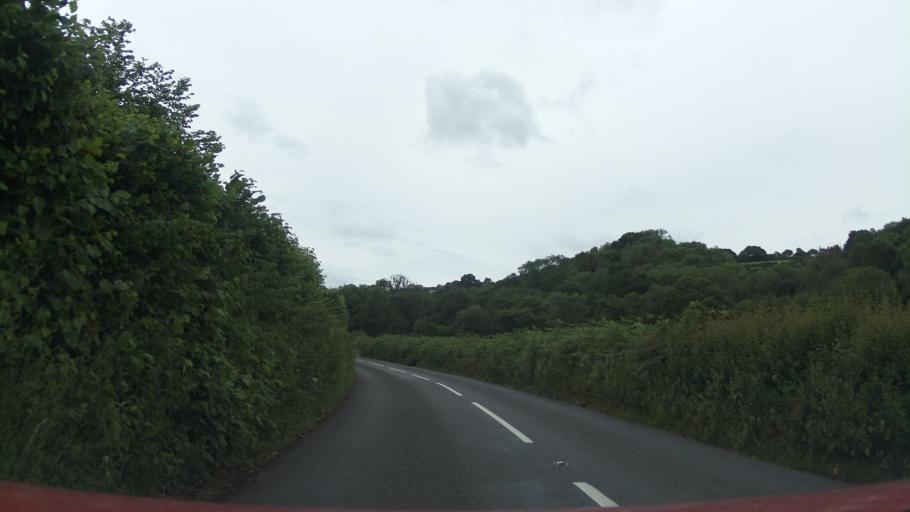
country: GB
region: England
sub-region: Devon
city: Chudleigh
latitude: 50.6304
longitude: -3.6399
